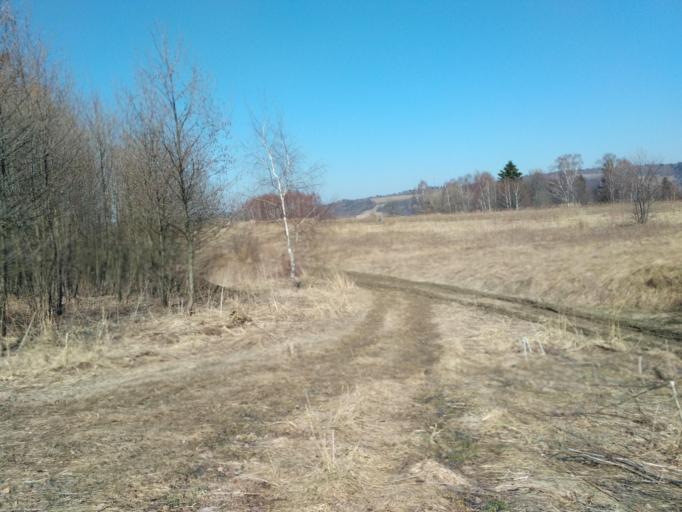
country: PL
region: Subcarpathian Voivodeship
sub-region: Powiat brzozowski
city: Golcowa
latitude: 49.7621
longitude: 22.0315
